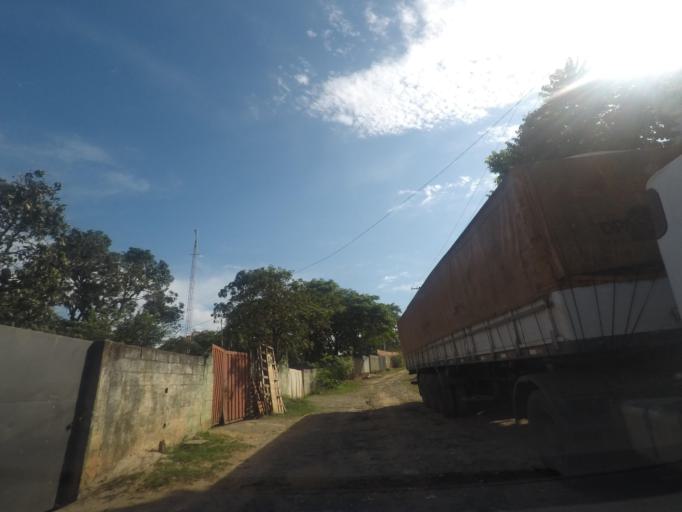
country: BR
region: Sao Paulo
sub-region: Sumare
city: Sumare
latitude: -22.7907
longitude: -47.2319
